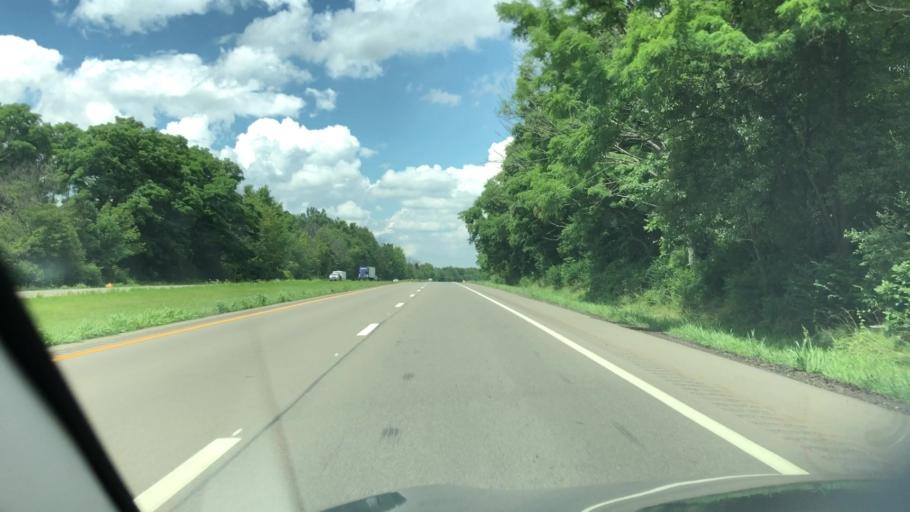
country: US
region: Ohio
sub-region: Stark County
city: Massillon
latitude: 40.8276
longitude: -81.5417
